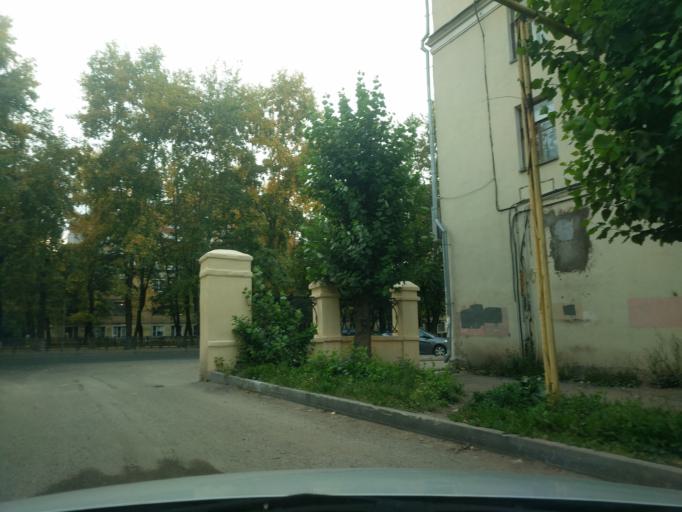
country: RU
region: Kirov
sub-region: Kirovo-Chepetskiy Rayon
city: Kirov
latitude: 58.6100
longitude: 49.6578
